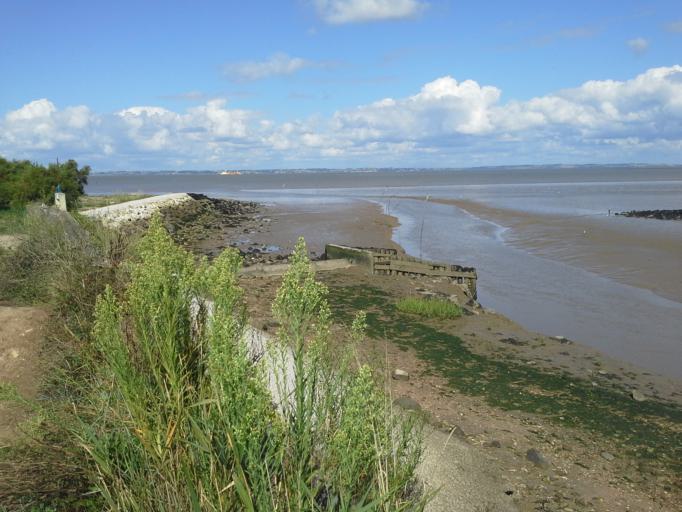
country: FR
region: Aquitaine
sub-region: Departement de la Gironde
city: Gaillan-en-Medoc
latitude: 45.4256
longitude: -0.9199
